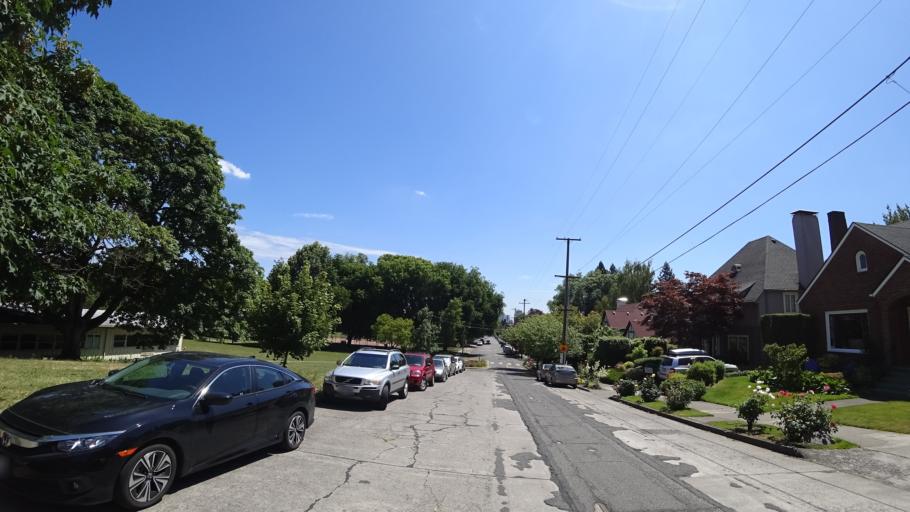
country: US
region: Oregon
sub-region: Multnomah County
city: Portland
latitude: 45.5325
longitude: -122.7057
